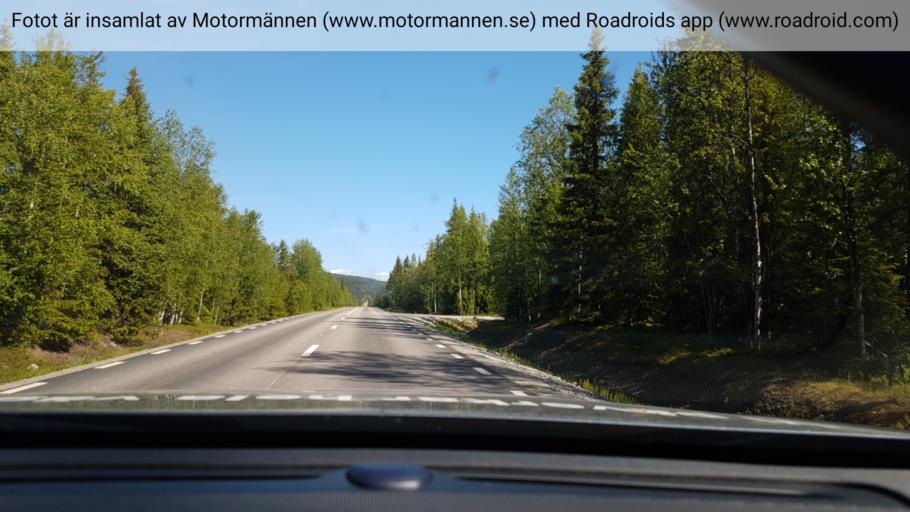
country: SE
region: Vaesterbotten
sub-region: Asele Kommun
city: Insjon
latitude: 64.7241
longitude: 17.6072
